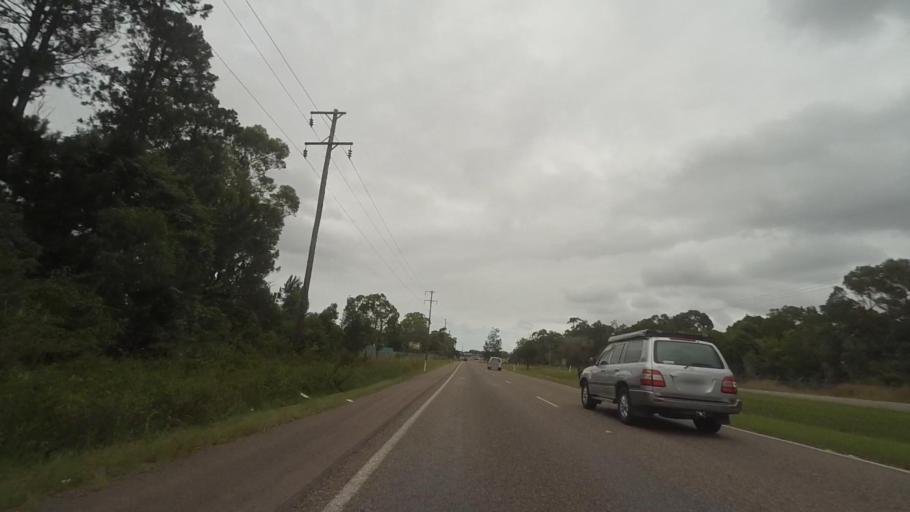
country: AU
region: New South Wales
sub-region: Wyong Shire
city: Buff Point
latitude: -33.1922
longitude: 151.5275
